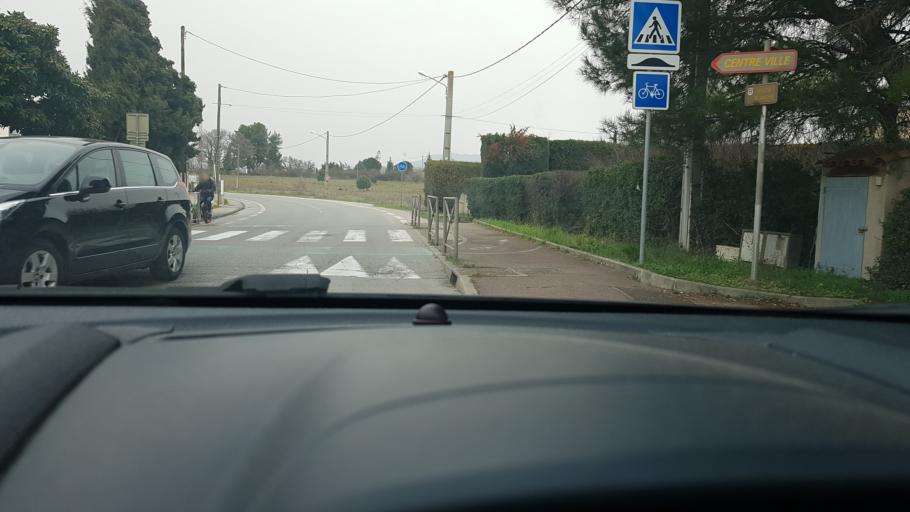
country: FR
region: Provence-Alpes-Cote d'Azur
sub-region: Departement des Bouches-du-Rhone
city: Gardanne
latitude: 43.4440
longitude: 5.4728
